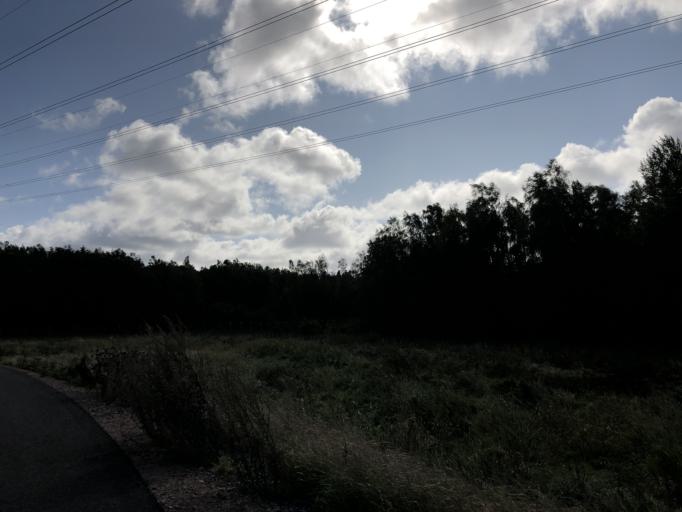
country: SE
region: Vaestra Goetaland
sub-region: Goteborg
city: Majorna
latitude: 57.7379
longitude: 11.8591
